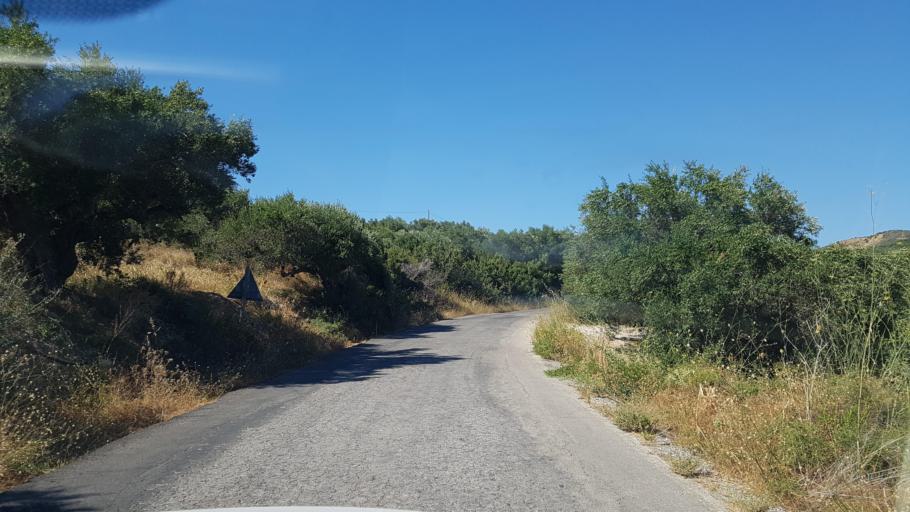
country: GR
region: Crete
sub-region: Nomos Chanias
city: Kissamos
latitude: 35.4973
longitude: 23.7221
